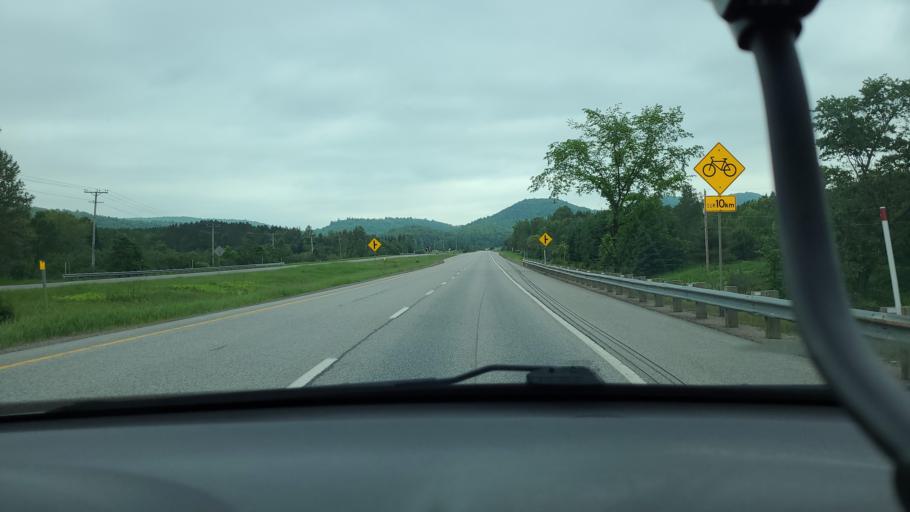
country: CA
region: Quebec
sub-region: Laurentides
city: Labelle
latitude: 46.1793
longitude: -74.7271
